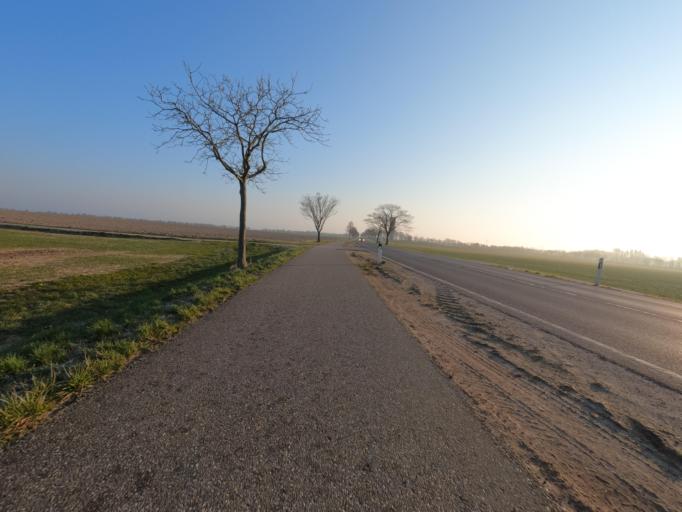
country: DE
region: North Rhine-Westphalia
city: Huckelhoven
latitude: 51.0705
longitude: 6.2636
